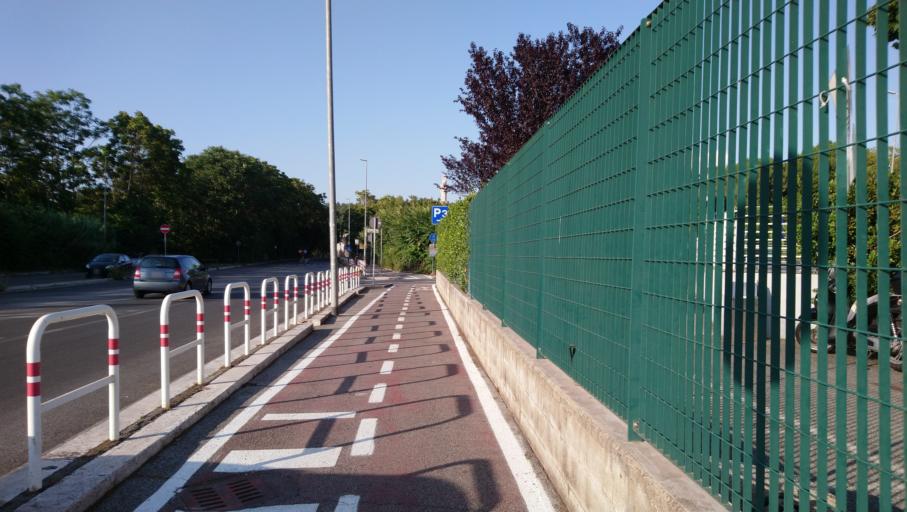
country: IT
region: Latium
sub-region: Citta metropolitana di Roma Capitale
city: Rome
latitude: 41.9330
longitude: 12.4924
